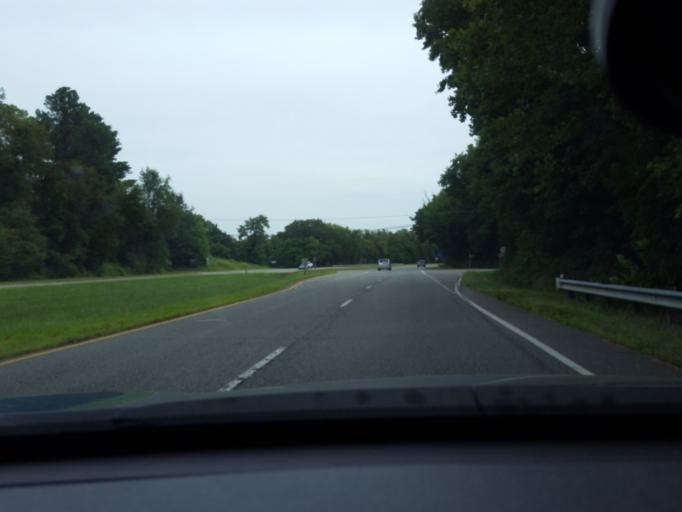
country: US
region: Virginia
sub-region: Caroline County
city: Bowling Green
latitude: 38.0512
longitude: -77.3414
